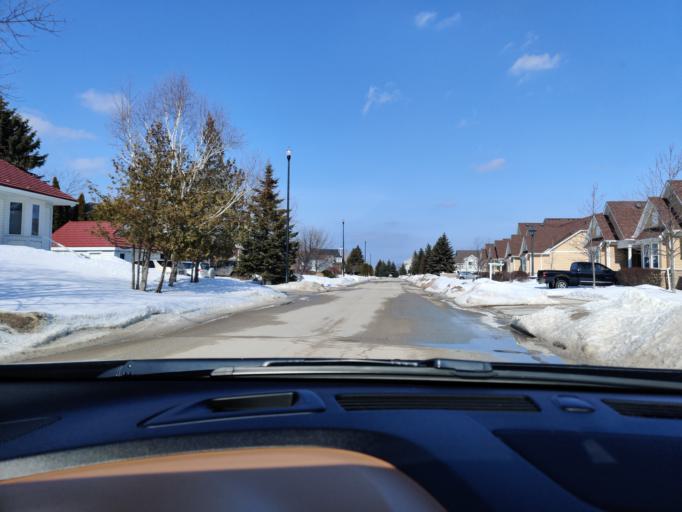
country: CA
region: Ontario
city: Collingwood
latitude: 44.5100
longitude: -80.2364
